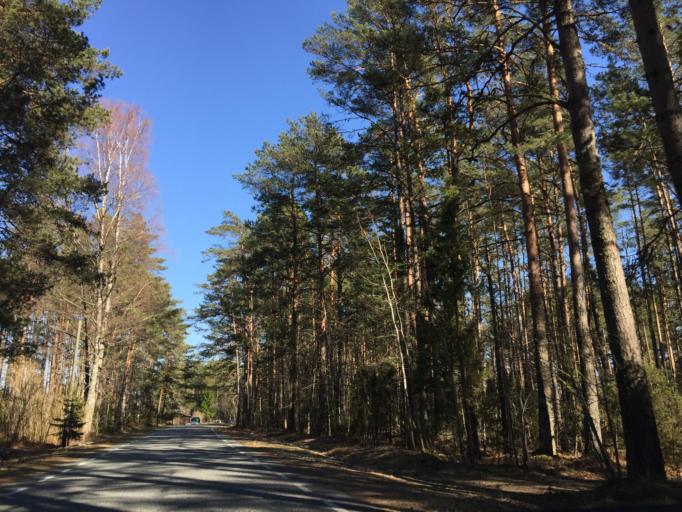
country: EE
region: Ida-Virumaa
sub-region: Johvi vald
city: Johvi
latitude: 59.0042
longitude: 27.3593
